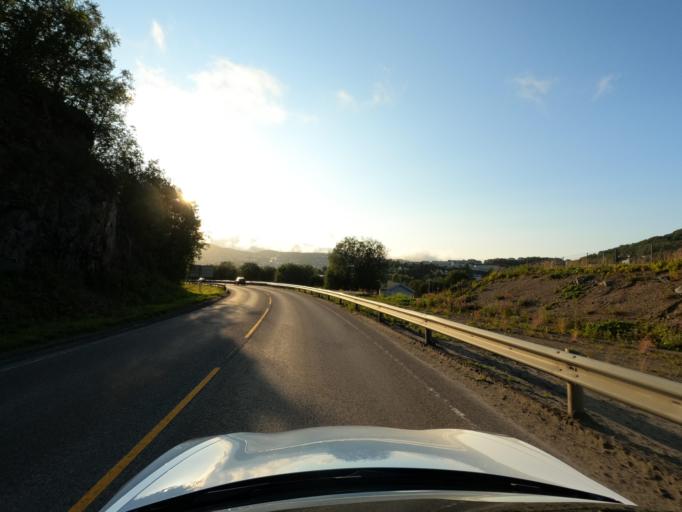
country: NO
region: Troms
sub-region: Harstad
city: Harstad
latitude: 68.7830
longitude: 16.5627
